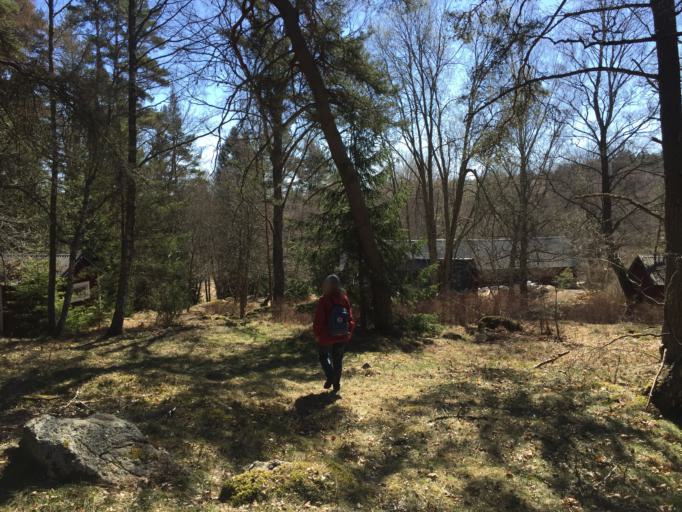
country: SE
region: Stockholm
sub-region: Salems Kommun
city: Ronninge
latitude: 59.2029
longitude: 17.7169
